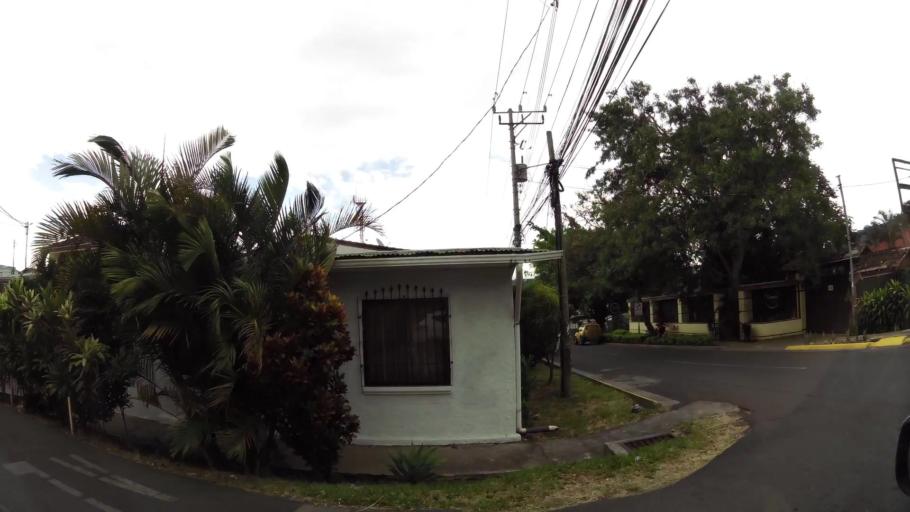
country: CR
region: San Jose
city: Santa Ana
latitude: 9.9329
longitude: -84.1801
